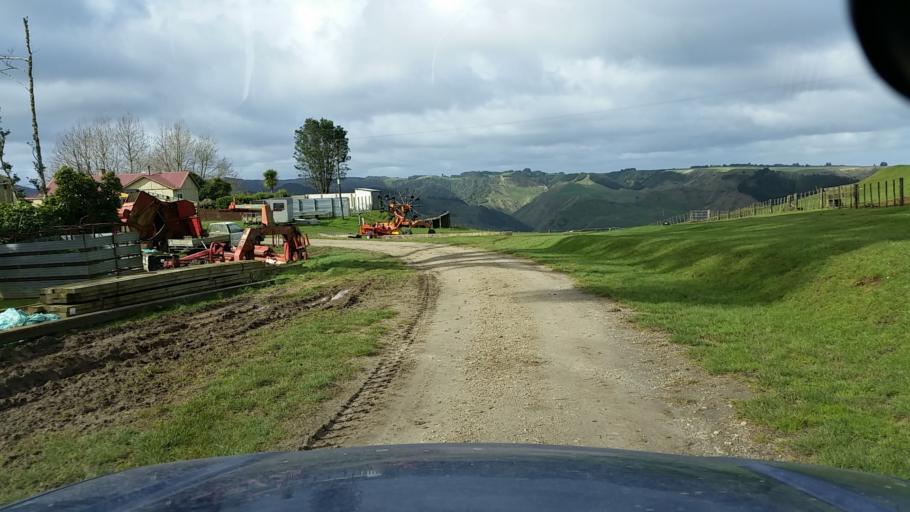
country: NZ
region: Taranaki
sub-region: South Taranaki District
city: Patea
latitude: -39.6578
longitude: 174.5702
